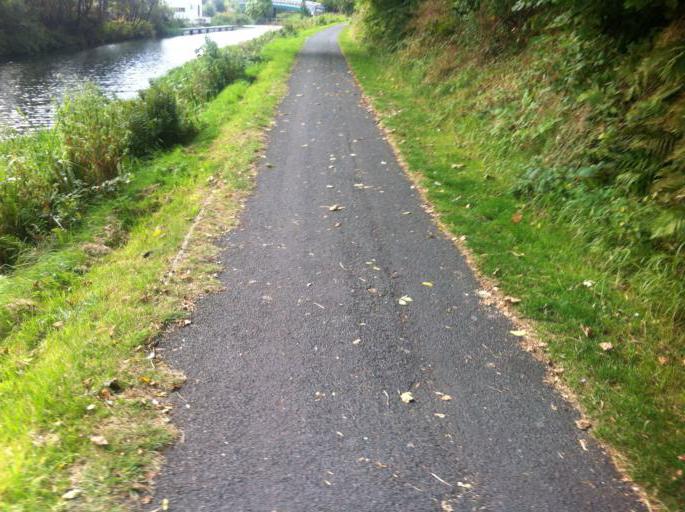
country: GB
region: Scotland
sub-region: East Dunbartonshire
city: Kirkintilloch
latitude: 55.9361
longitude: -4.1584
